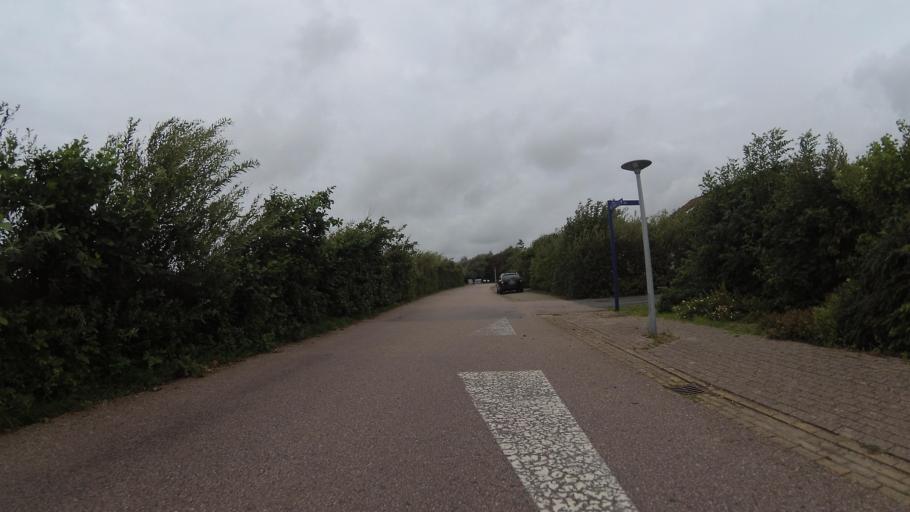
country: NL
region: North Holland
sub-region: Gemeente Den Helder
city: Den Helder
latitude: 52.8873
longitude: 4.7271
